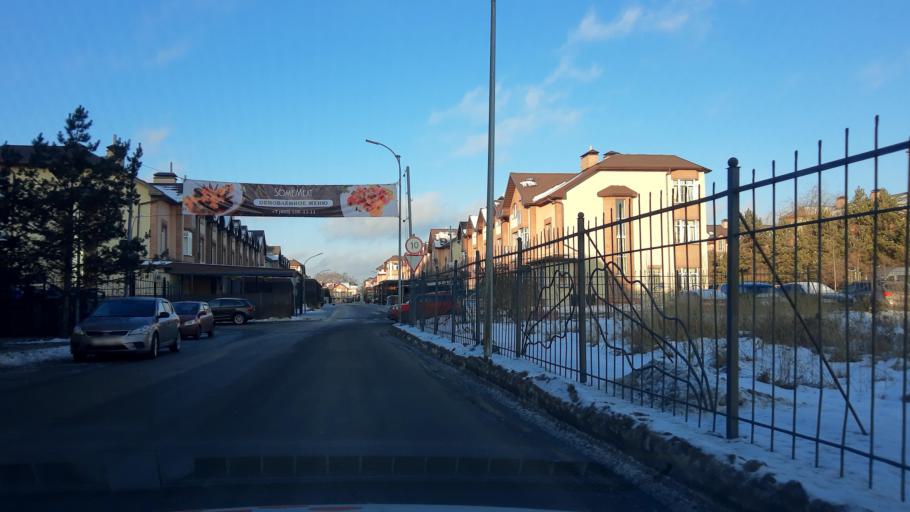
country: RU
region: Moskovskaya
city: Kommunarka
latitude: 55.5686
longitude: 37.4475
